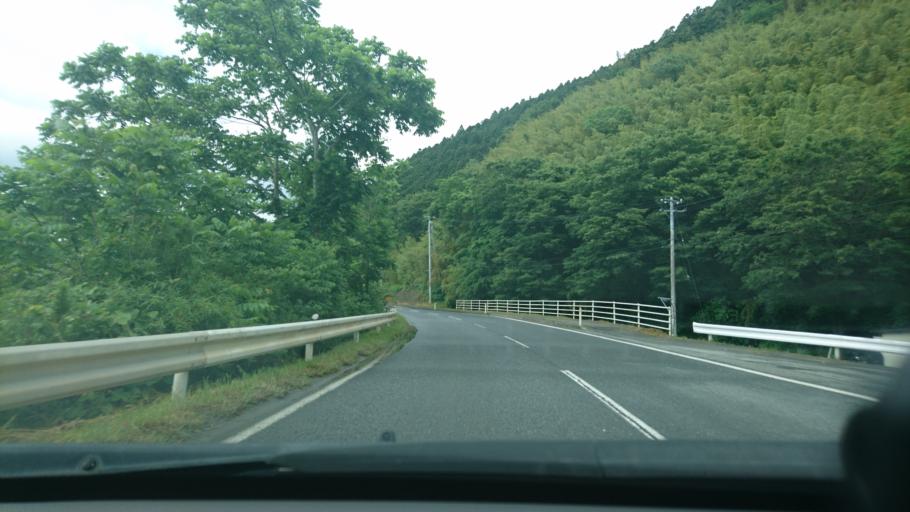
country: JP
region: Miyagi
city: Ishinomaki
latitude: 38.5937
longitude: 141.3049
